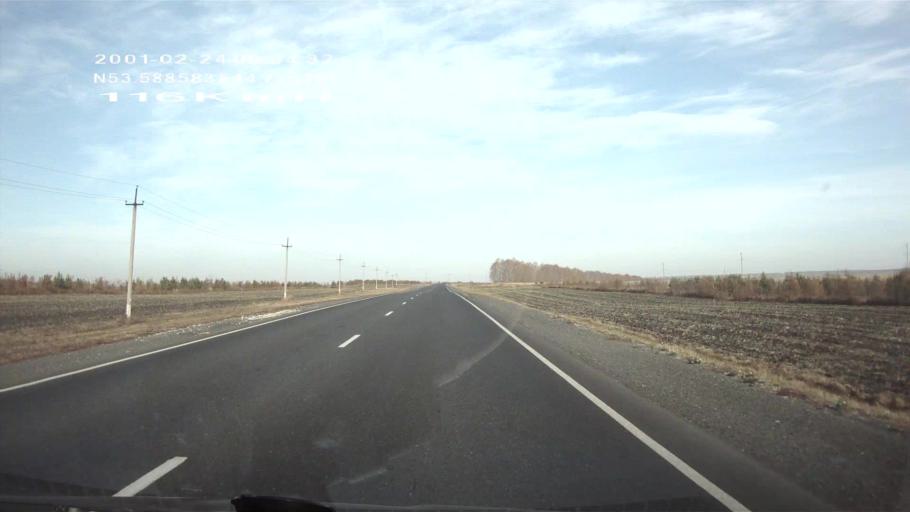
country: RU
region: Penza
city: Mokshan
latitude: 53.5876
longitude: 44.7265
